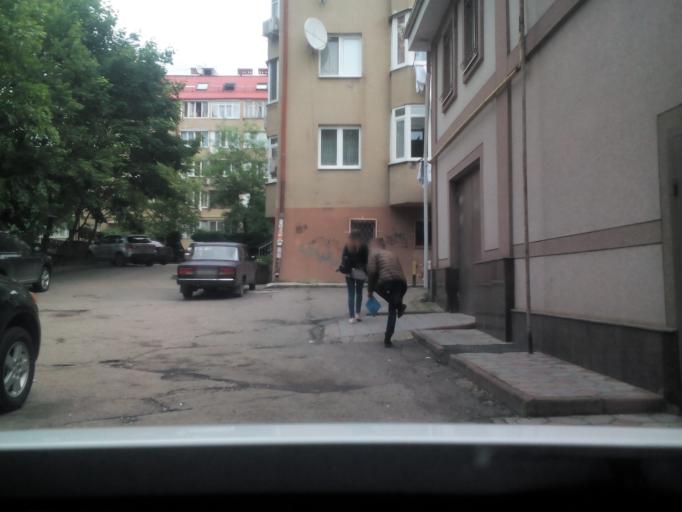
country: RU
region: Stavropol'skiy
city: Pyatigorsk
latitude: 44.0457
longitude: 43.0641
